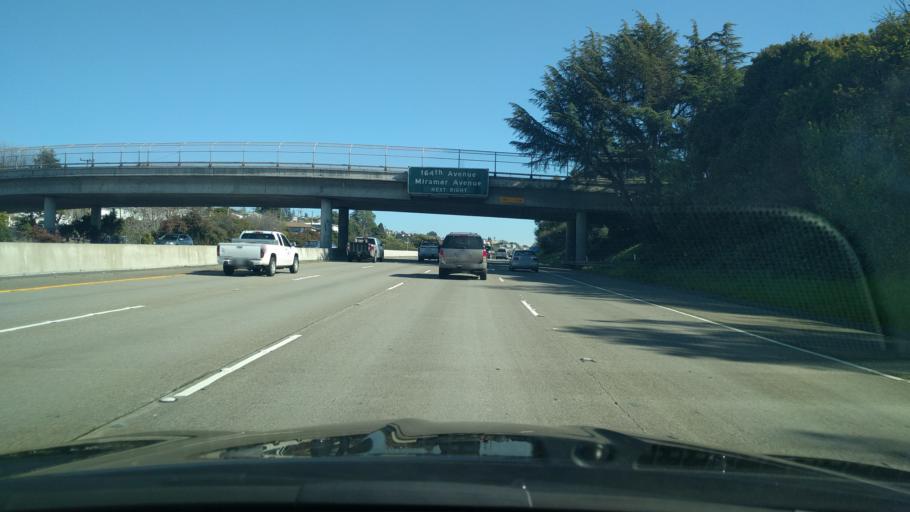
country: US
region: California
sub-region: Alameda County
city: Ashland
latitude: 37.7055
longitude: -122.1175
